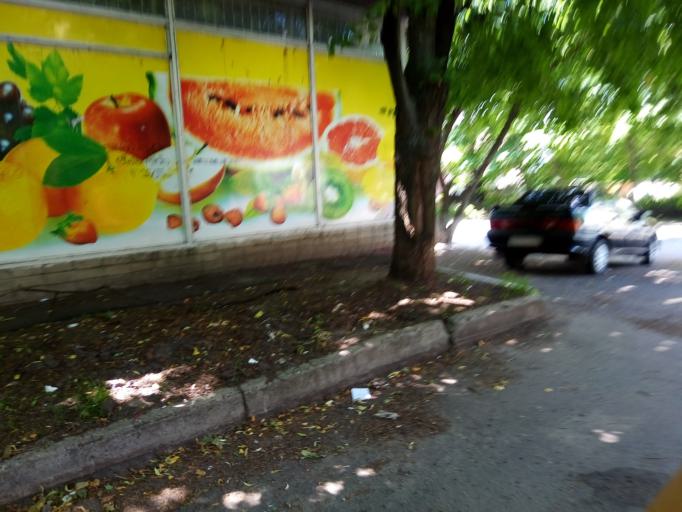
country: RU
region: Kursk
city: Kursk
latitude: 51.7441
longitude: 36.1834
